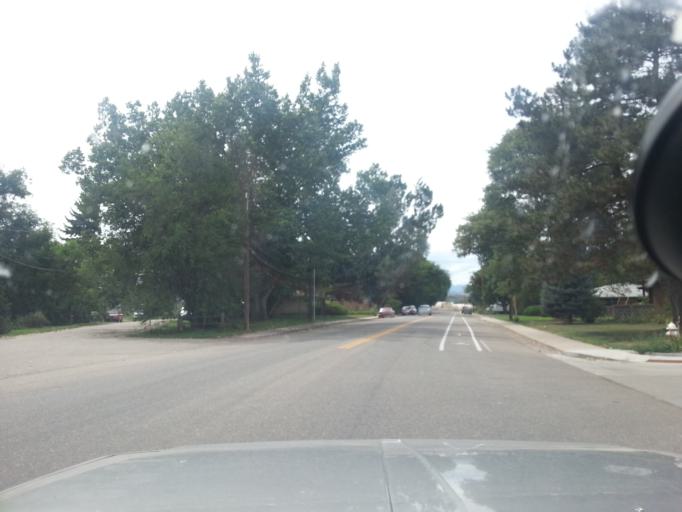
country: US
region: Colorado
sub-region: Larimer County
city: Loveland
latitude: 40.4000
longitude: -105.0996
